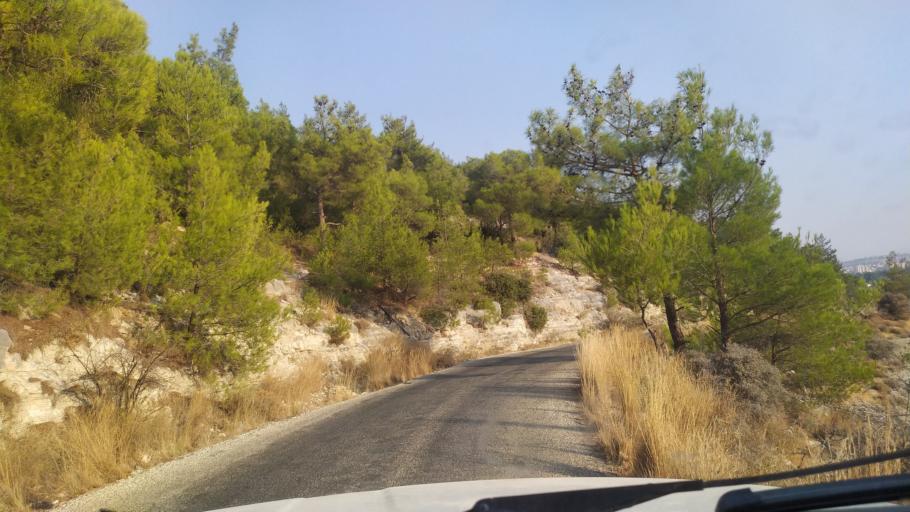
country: TR
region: Mersin
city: Silifke
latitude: 36.4049
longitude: 33.9242
